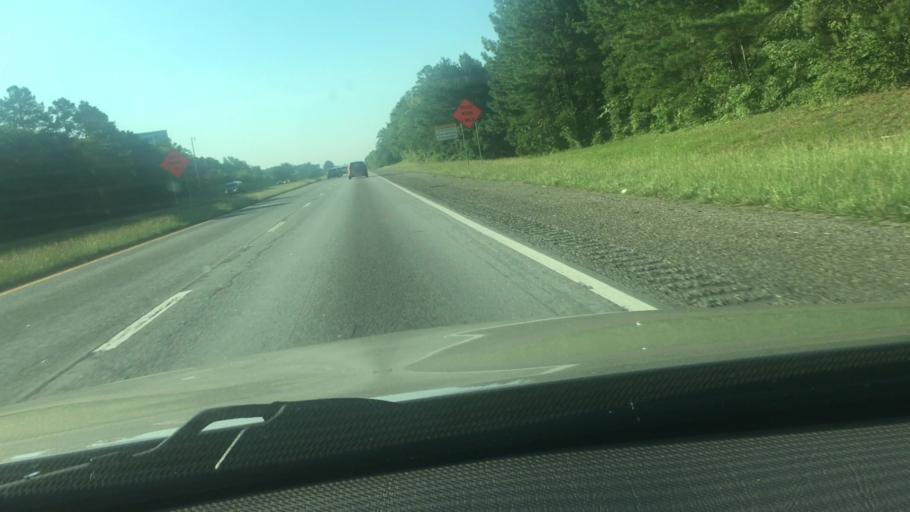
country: US
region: South Carolina
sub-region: Lexington County
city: Irmo
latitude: 34.1178
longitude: -81.1945
